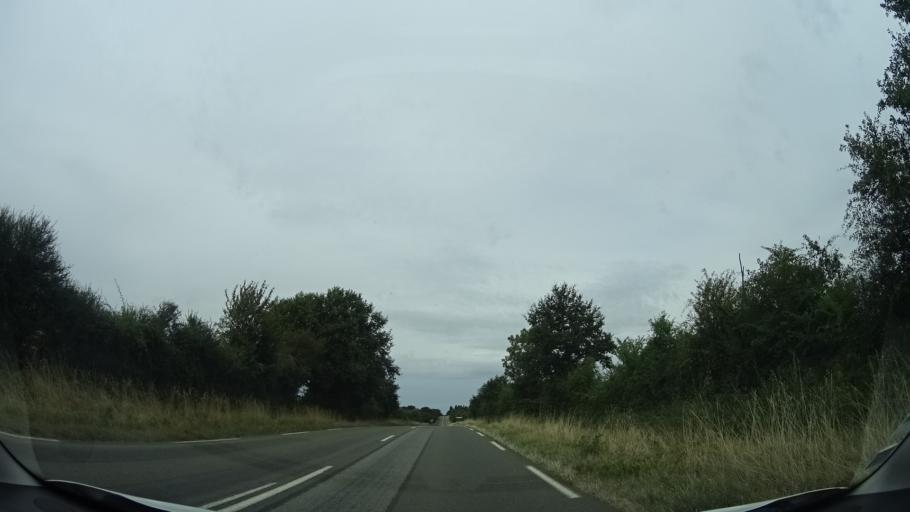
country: FR
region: Pays de la Loire
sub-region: Departement de la Mayenne
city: Meslay-du-Maine
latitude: 47.9358
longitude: -0.5062
